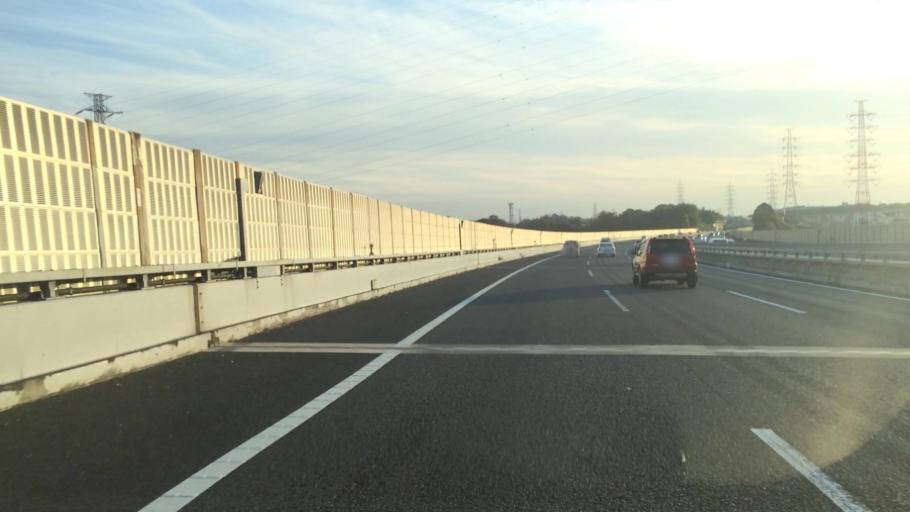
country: JP
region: Kanagawa
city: Yokohama
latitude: 35.5559
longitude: 139.6085
